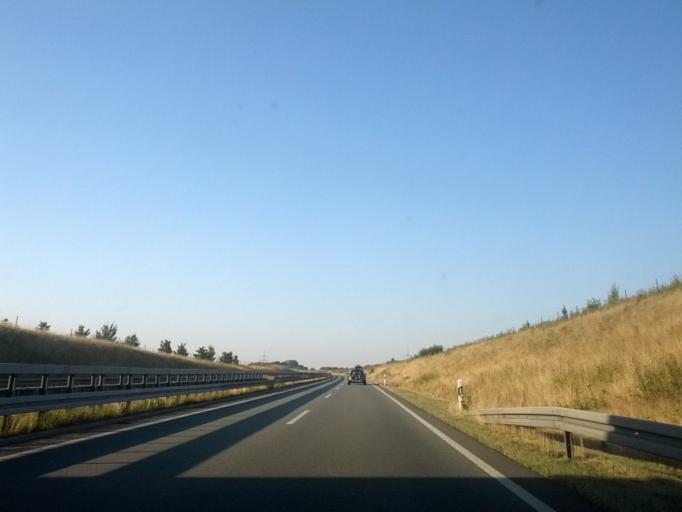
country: DE
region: Mecklenburg-Vorpommern
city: Brandshagen
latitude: 54.2177
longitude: 13.1520
